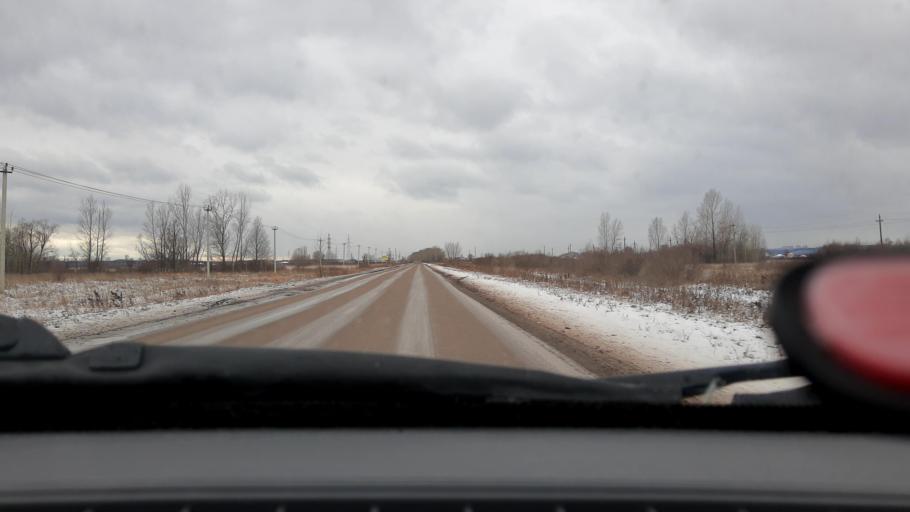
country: RU
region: Bashkortostan
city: Kabakovo
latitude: 54.6818
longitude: 56.1225
